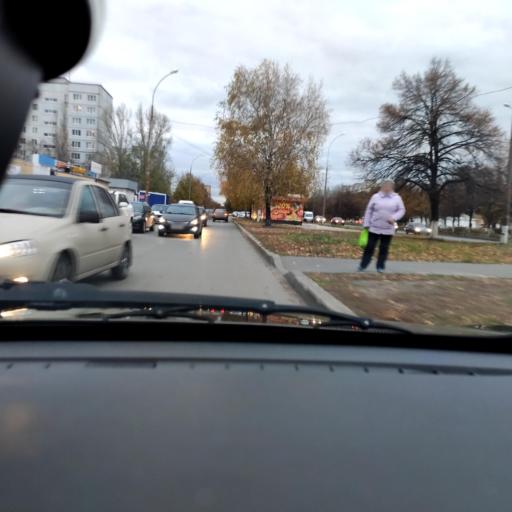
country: RU
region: Samara
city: Tol'yatti
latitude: 53.5332
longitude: 49.3139
